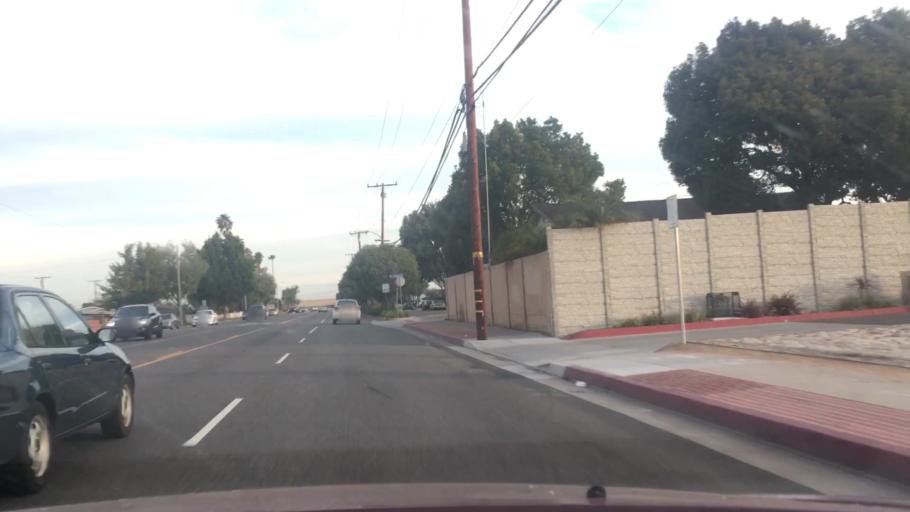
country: US
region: California
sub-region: Orange County
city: Buena Park
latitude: 33.8506
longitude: -118.0024
